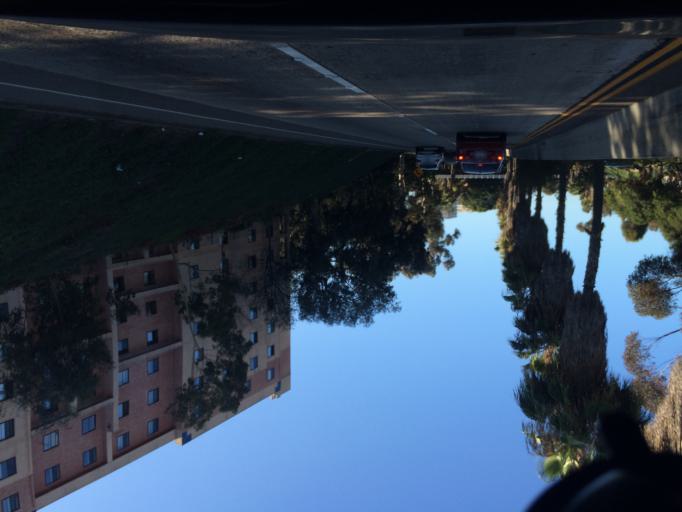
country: US
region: California
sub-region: San Diego County
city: San Diego
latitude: 32.7483
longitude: -117.1560
